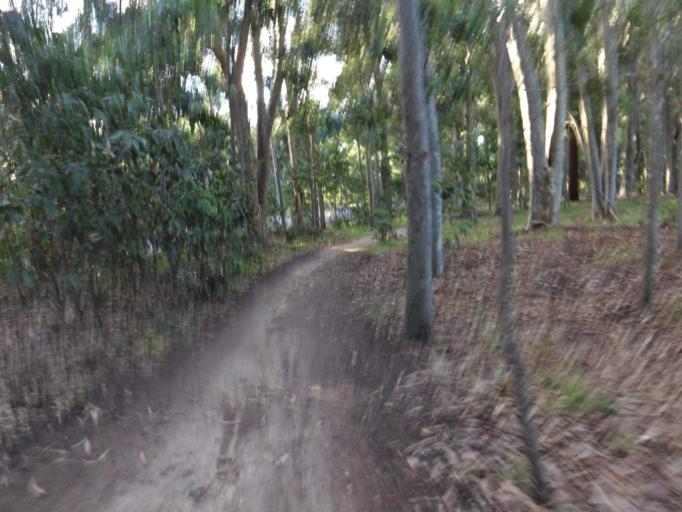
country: AU
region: Victoria
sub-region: Casey
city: Narre Warren North
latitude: -37.9675
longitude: 145.3029
